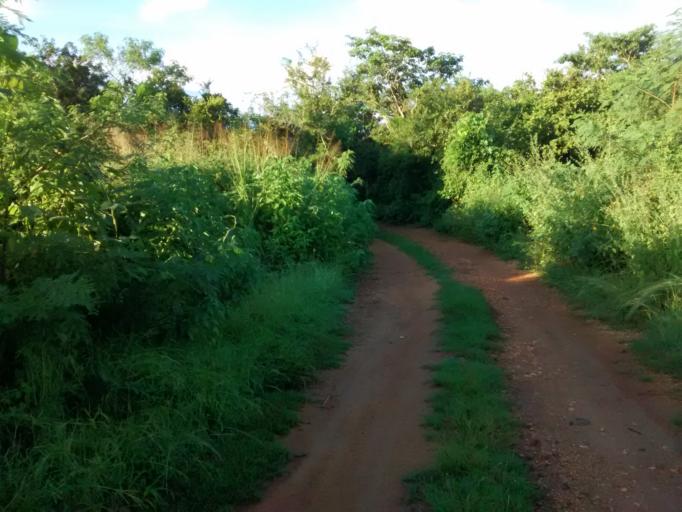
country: MX
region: Yucatan
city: Valladolid
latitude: 20.7092
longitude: -88.2062
